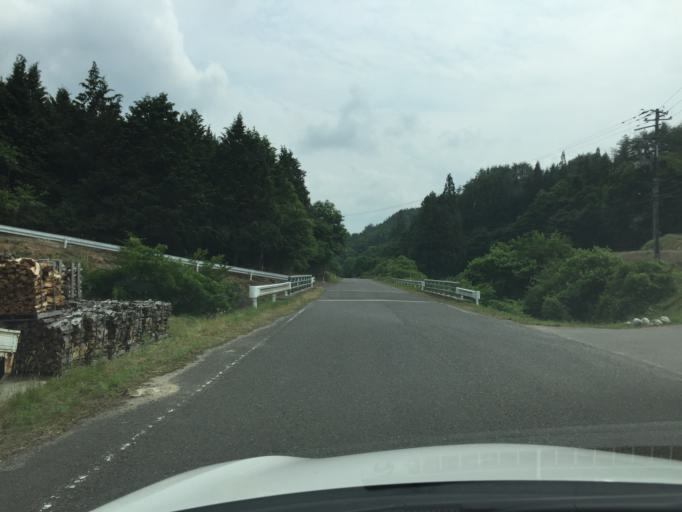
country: JP
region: Fukushima
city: Ishikawa
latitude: 37.2291
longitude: 140.4917
